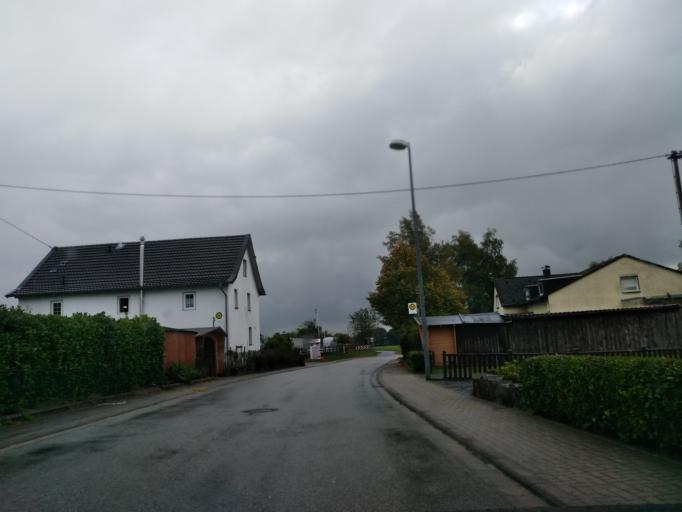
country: DE
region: Rheinland-Pfalz
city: Asbach
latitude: 50.6787
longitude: 7.4353
